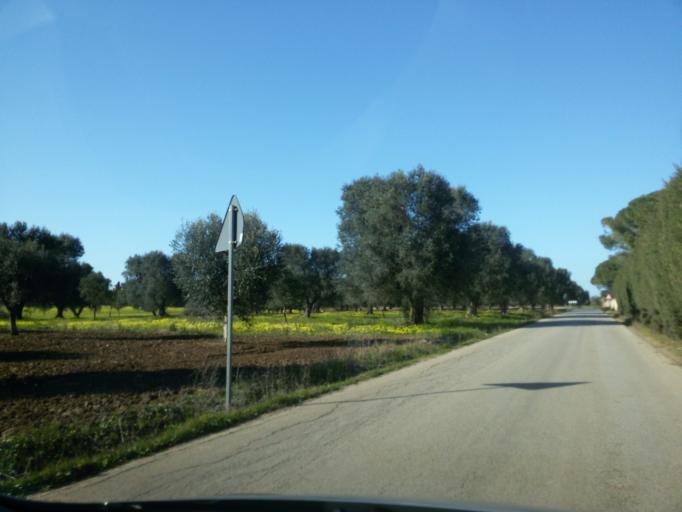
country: IT
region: Apulia
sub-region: Provincia di Brindisi
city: Mesagne
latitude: 40.6585
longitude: 17.8239
